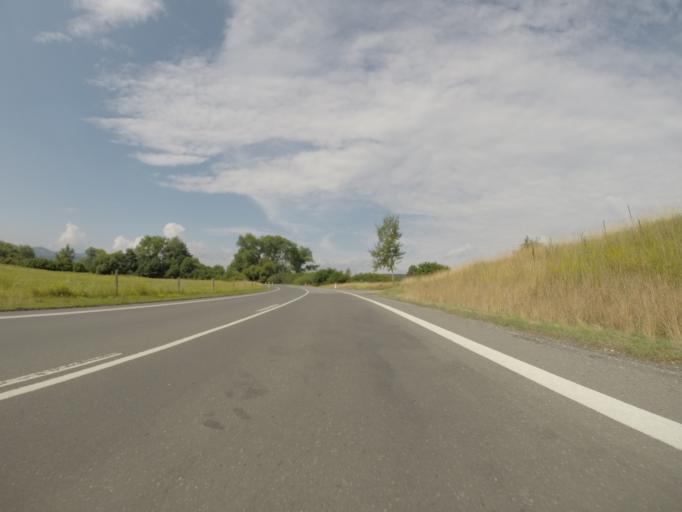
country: SK
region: Banskobystricky
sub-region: Okres Banska Bystrica
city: Zvolen
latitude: 48.6077
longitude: 19.1171
